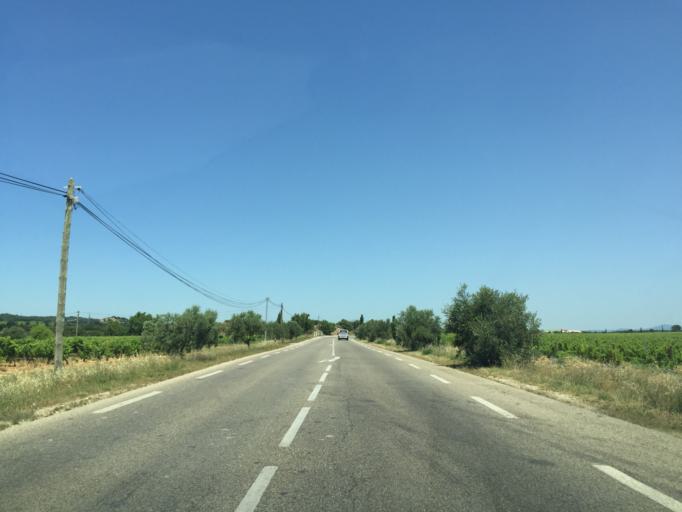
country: FR
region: Provence-Alpes-Cote d'Azur
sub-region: Departement du Vaucluse
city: Serignan-du-Comtat
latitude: 44.2082
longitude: 4.8688
